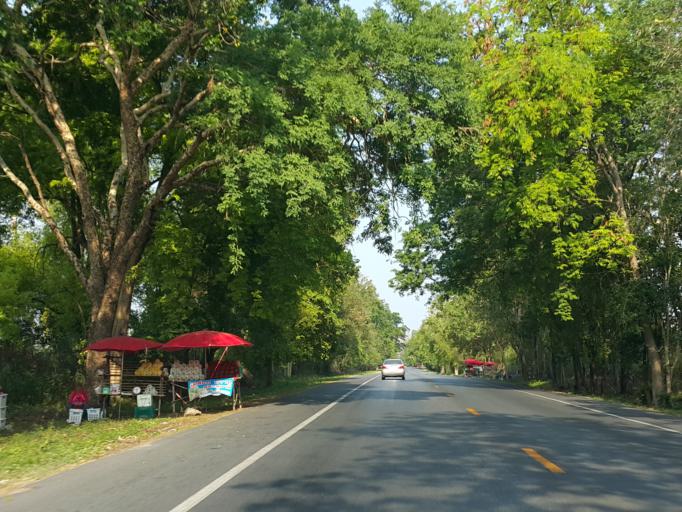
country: TH
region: Kanchanaburi
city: Sai Yok
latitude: 14.0899
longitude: 99.2974
